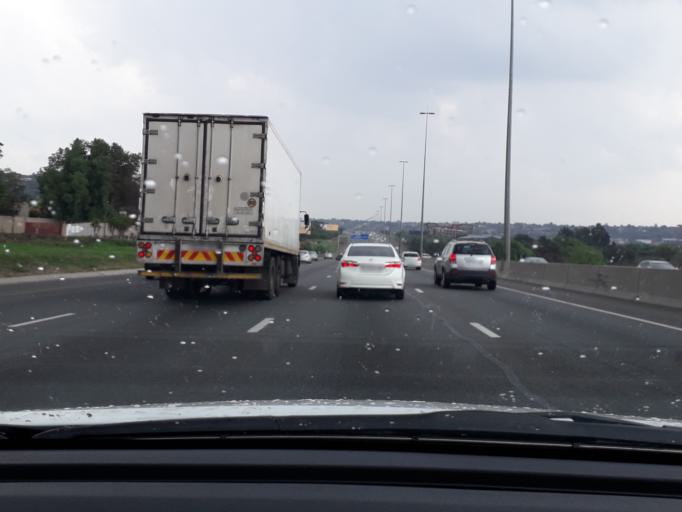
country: ZA
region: Gauteng
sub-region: City of Johannesburg Metropolitan Municipality
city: Roodepoort
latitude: -26.1404
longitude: 27.9331
